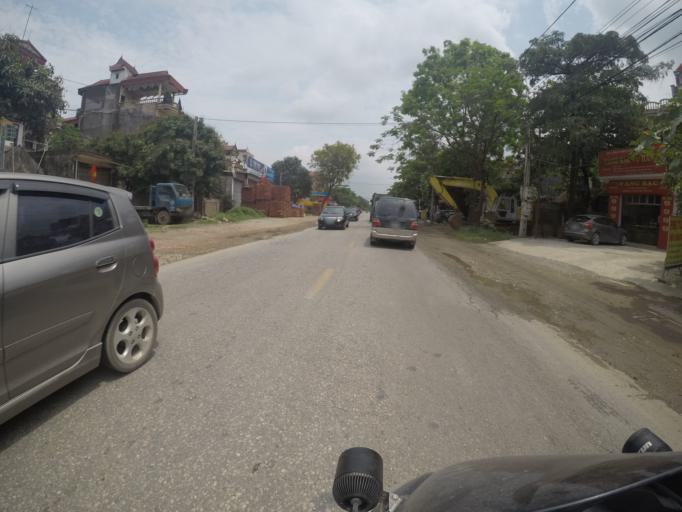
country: VN
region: Ha Noi
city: Soc Son
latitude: 21.2258
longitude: 105.8490
